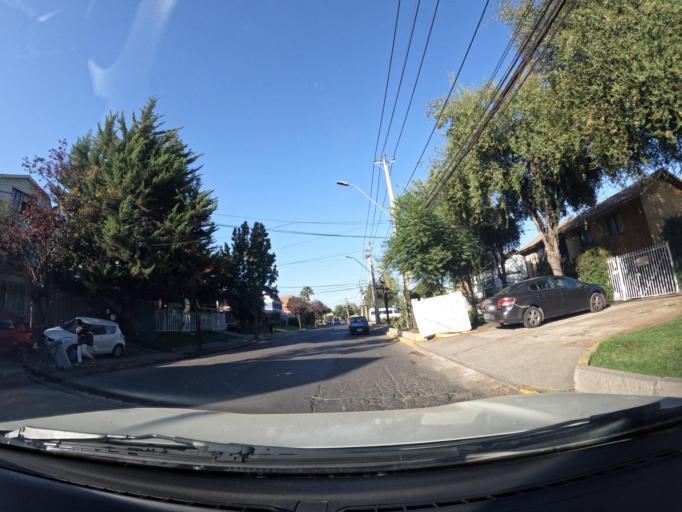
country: CL
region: Santiago Metropolitan
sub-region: Provincia de Santiago
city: Villa Presidente Frei, Nunoa, Santiago, Chile
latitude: -33.4799
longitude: -70.5389
